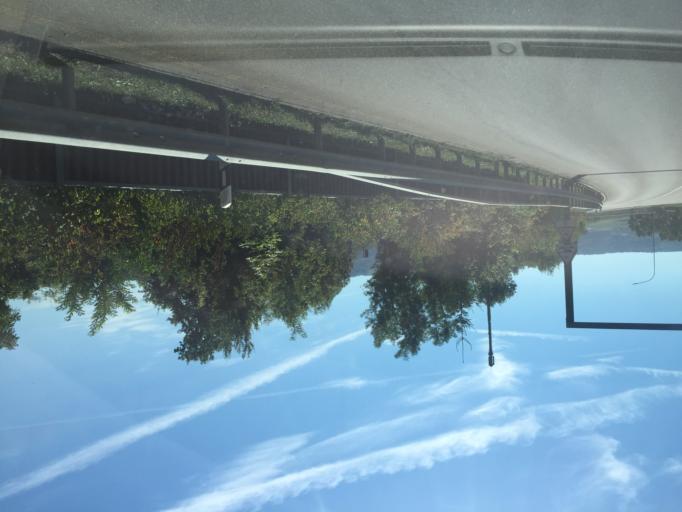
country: CH
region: Thurgau
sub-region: Frauenfeld District
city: Wagenhausen
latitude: 47.6748
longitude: 8.8356
